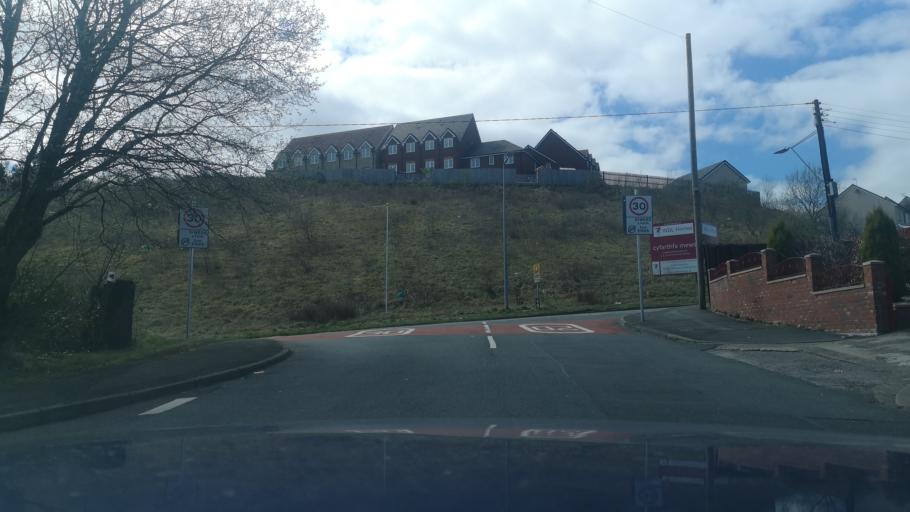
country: GB
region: Wales
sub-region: Merthyr Tydfil County Borough
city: Merthyr Tydfil
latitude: 51.7537
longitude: -3.4088
